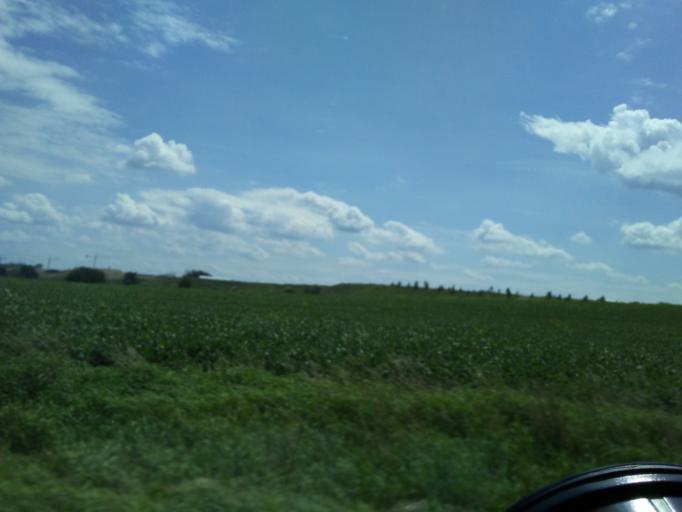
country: US
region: Wisconsin
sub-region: Dane County
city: Verona
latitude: 43.0130
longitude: -89.5701
